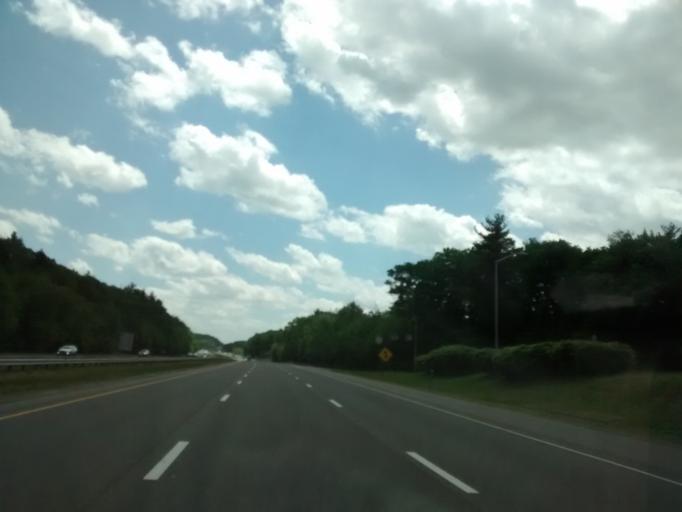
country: US
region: Massachusetts
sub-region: Hampden County
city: Holland
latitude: 41.9868
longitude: -72.1755
